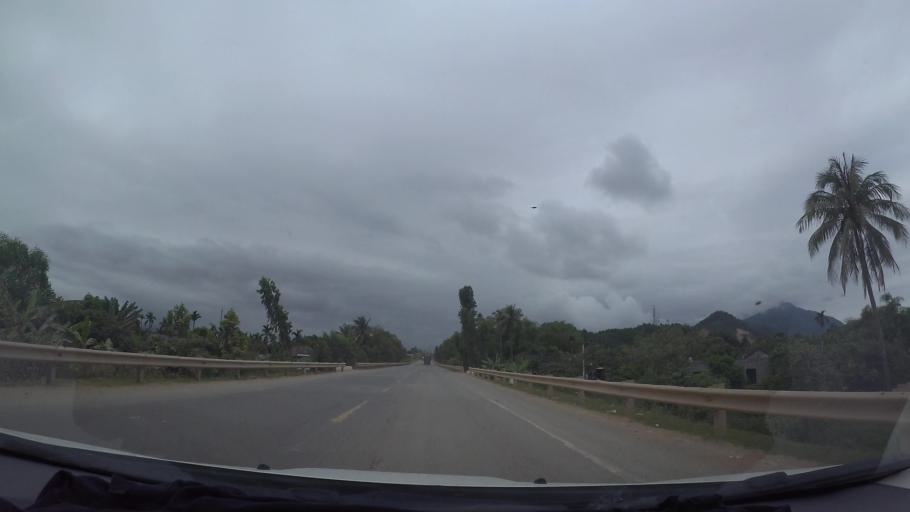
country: VN
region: Da Nang
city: Lien Chieu
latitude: 16.1047
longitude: 108.1002
